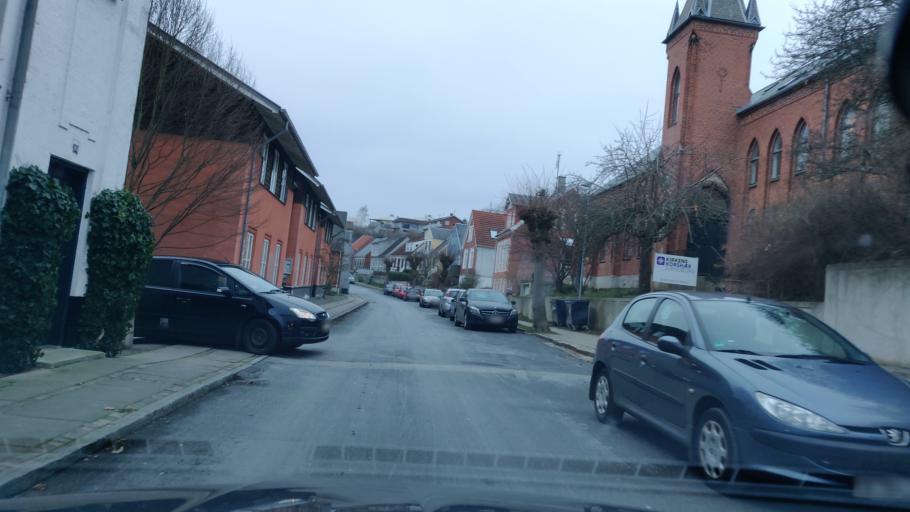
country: DK
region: South Denmark
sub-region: Svendborg Kommune
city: Svendborg
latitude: 55.0653
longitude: 10.6129
